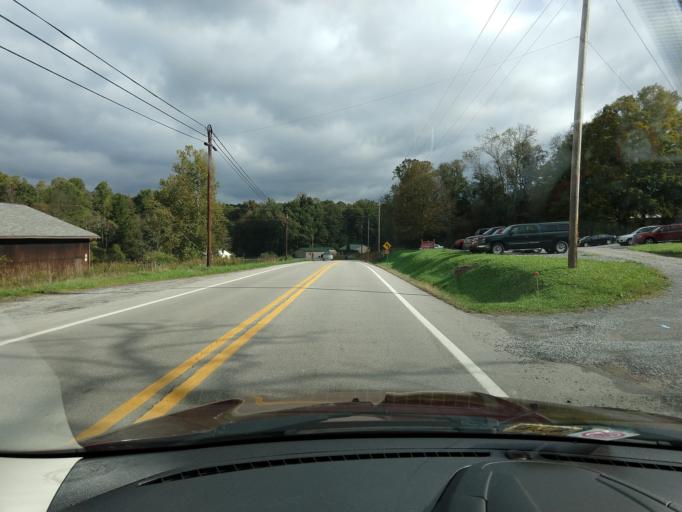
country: US
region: West Virginia
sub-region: Barbour County
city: Belington
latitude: 39.0083
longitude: -79.9389
